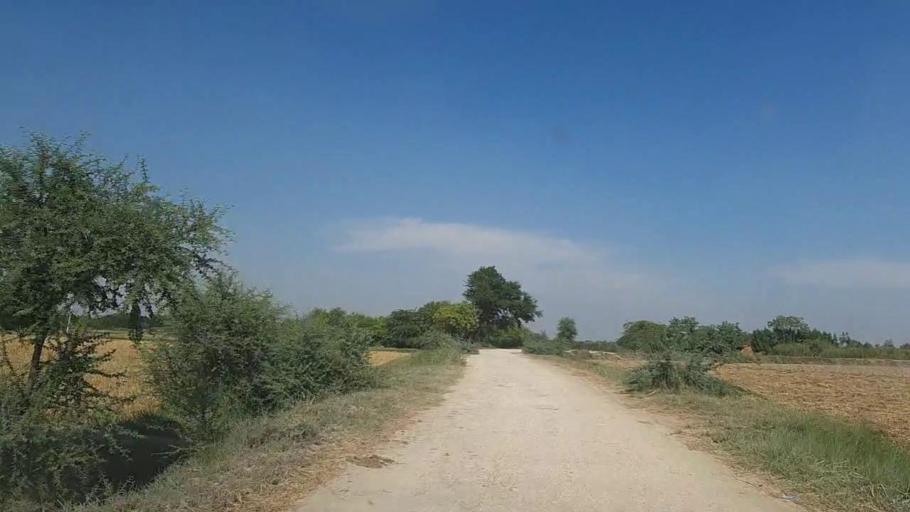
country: PK
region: Sindh
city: Mirpur Batoro
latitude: 24.7501
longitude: 68.2825
